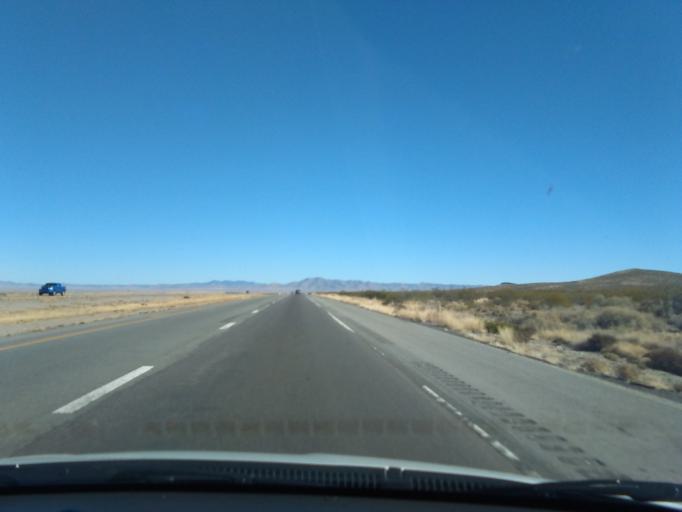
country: US
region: New Mexico
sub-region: Hidalgo County
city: Lordsburg
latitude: 32.3284
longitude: -108.7962
